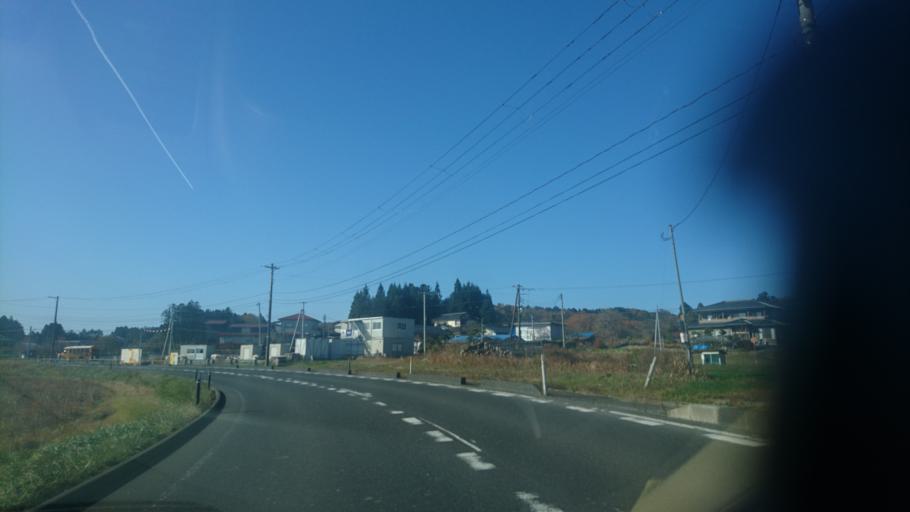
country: JP
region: Miyagi
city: Tomiya
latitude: 38.4205
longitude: 140.8844
